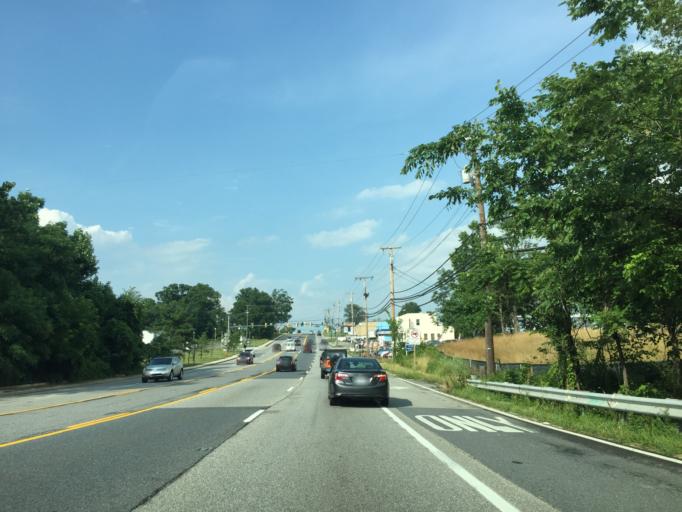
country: US
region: Maryland
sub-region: Howard County
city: West Elkridge
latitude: 39.1976
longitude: -76.7413
